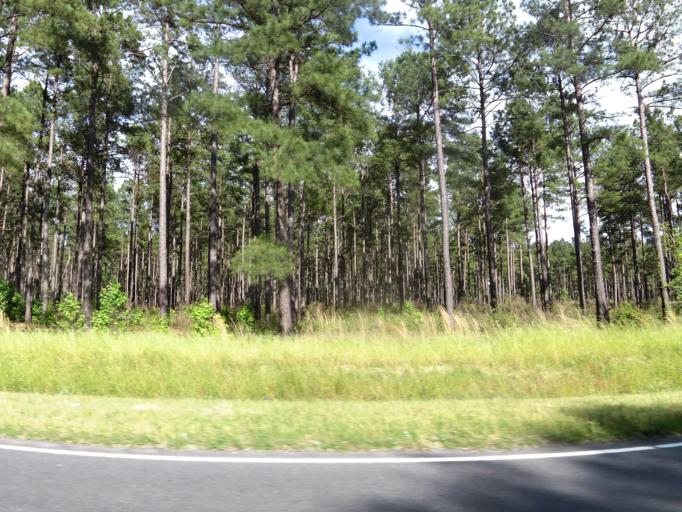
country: US
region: South Carolina
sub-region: Allendale County
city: Fairfax
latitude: 33.0086
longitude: -81.2181
